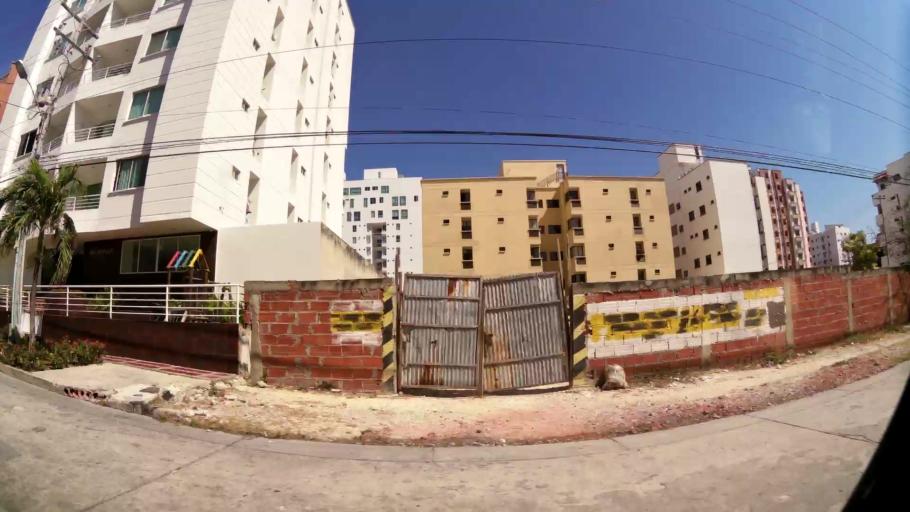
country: CO
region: Atlantico
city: Barranquilla
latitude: 11.0151
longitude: -74.8237
